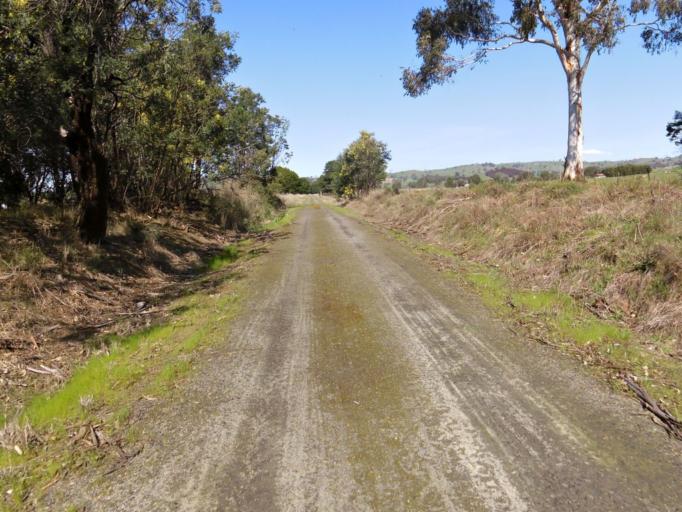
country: AU
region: Victoria
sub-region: Murrindindi
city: Alexandra
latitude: -37.0023
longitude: 145.7469
